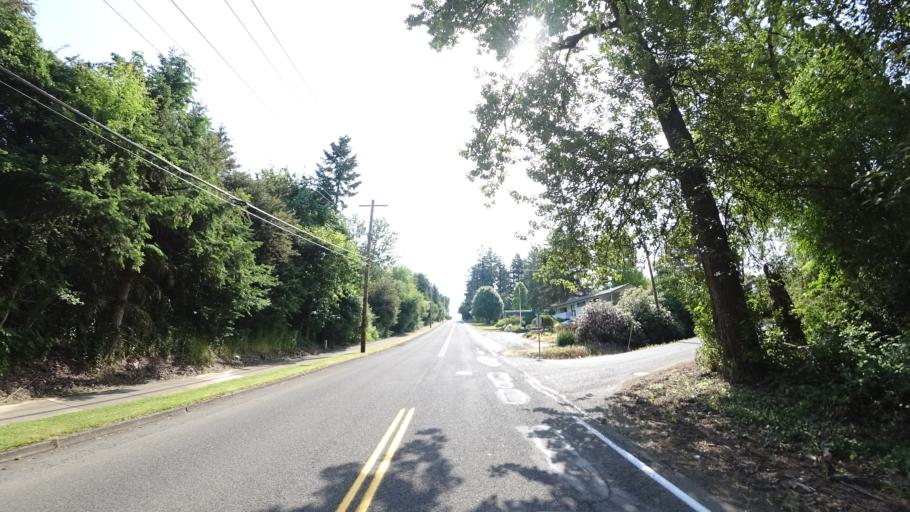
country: US
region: Oregon
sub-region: Clackamas County
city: Happy Valley
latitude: 45.4613
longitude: -122.5217
